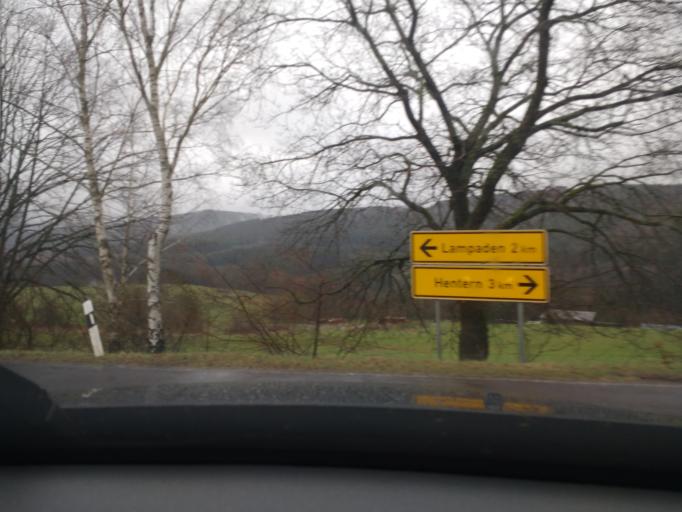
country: DE
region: Rheinland-Pfalz
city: Schomerich
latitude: 49.6326
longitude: 6.7098
